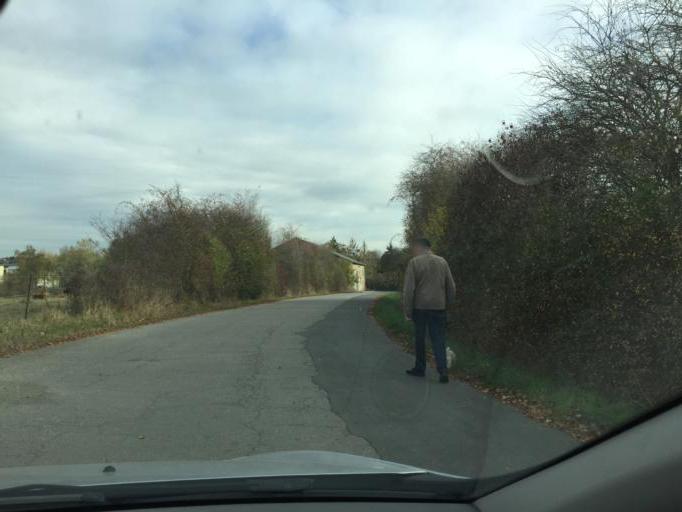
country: LU
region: Luxembourg
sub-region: Canton de Luxembourg
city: Bertrange
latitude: 49.6069
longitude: 6.0409
